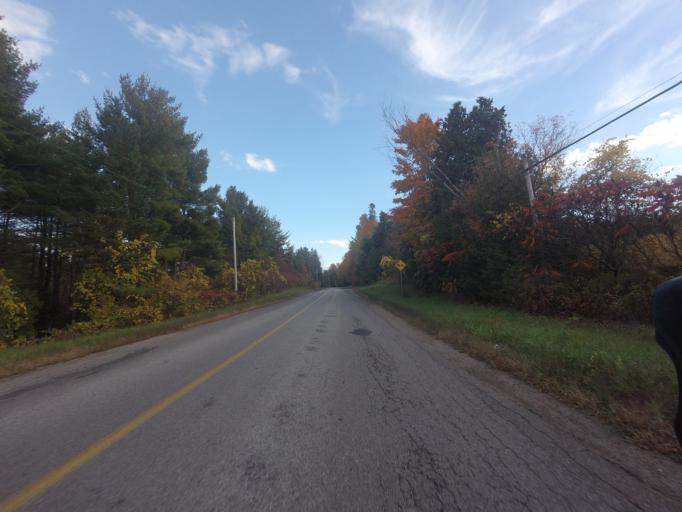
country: CA
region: Ontario
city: Pembroke
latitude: 45.5289
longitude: -77.0866
